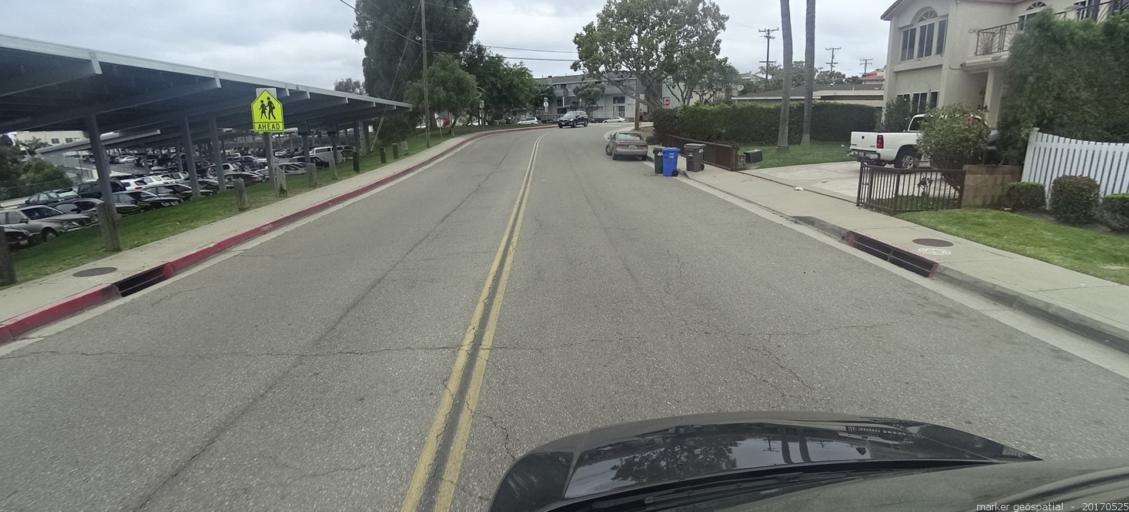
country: US
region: California
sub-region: Los Angeles County
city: Redondo Beach
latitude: 33.8485
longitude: -118.3817
